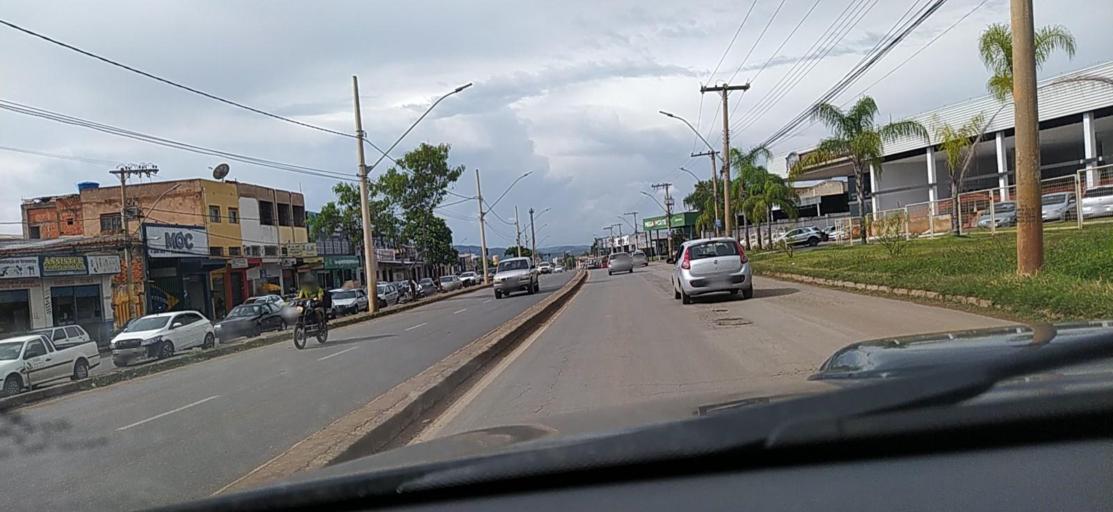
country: BR
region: Minas Gerais
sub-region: Montes Claros
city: Montes Claros
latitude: -16.7272
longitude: -43.8450
